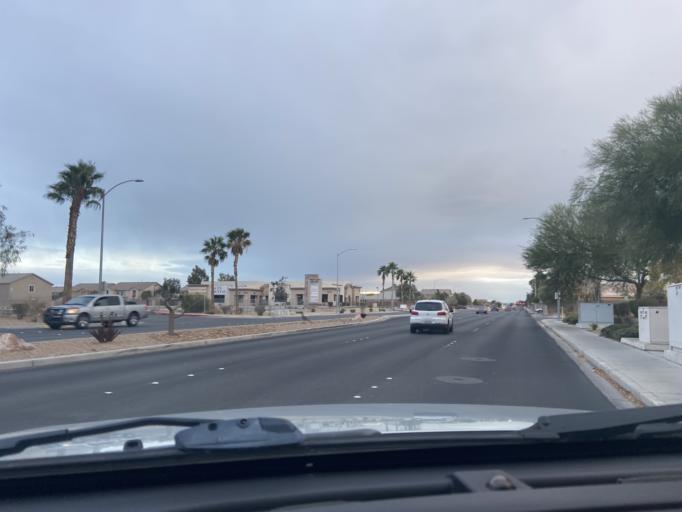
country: US
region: Nevada
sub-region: Clark County
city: North Las Vegas
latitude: 36.2383
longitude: -115.1802
